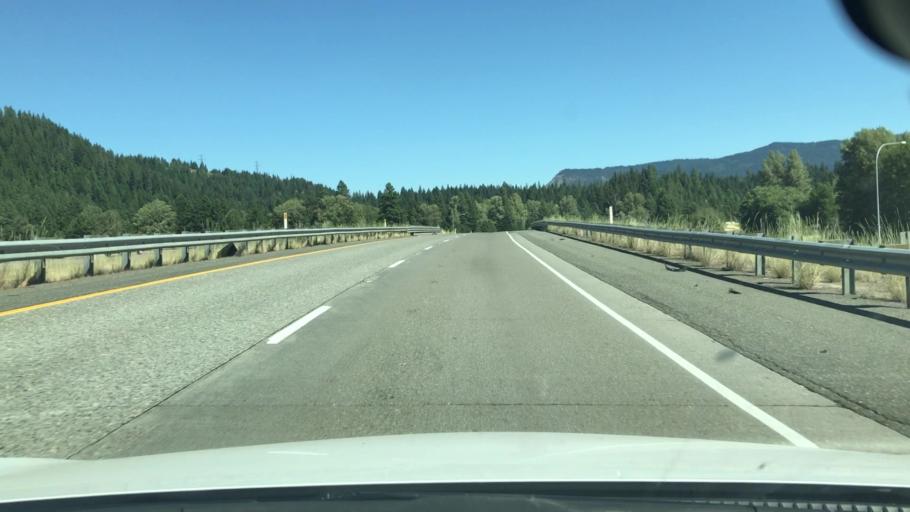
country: US
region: Washington
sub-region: Kittitas County
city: Cle Elum
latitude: 47.1951
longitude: -121.0534
